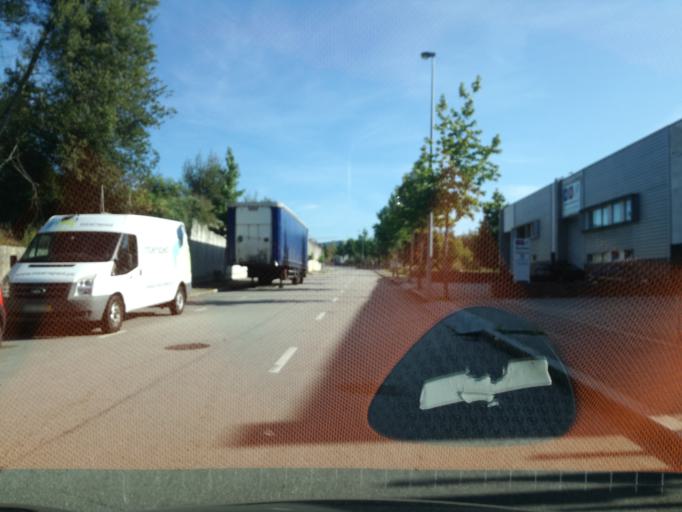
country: PT
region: Porto
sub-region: Maia
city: Anta
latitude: 41.2732
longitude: -8.6055
